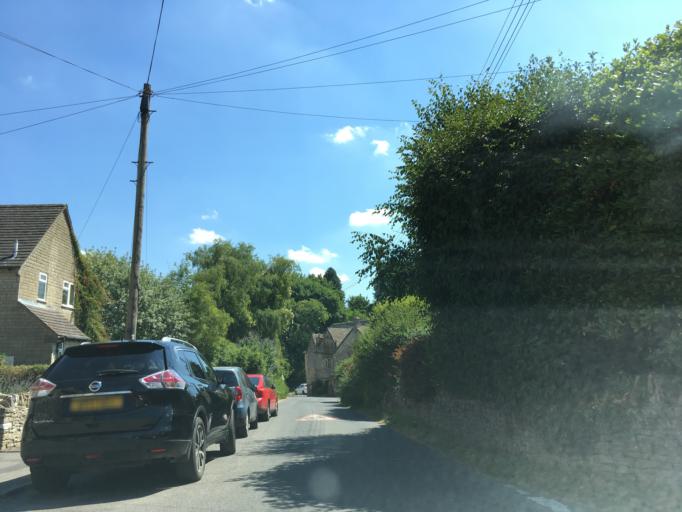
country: GB
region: England
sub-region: Gloucestershire
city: Chalford
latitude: 51.7536
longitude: -2.1423
